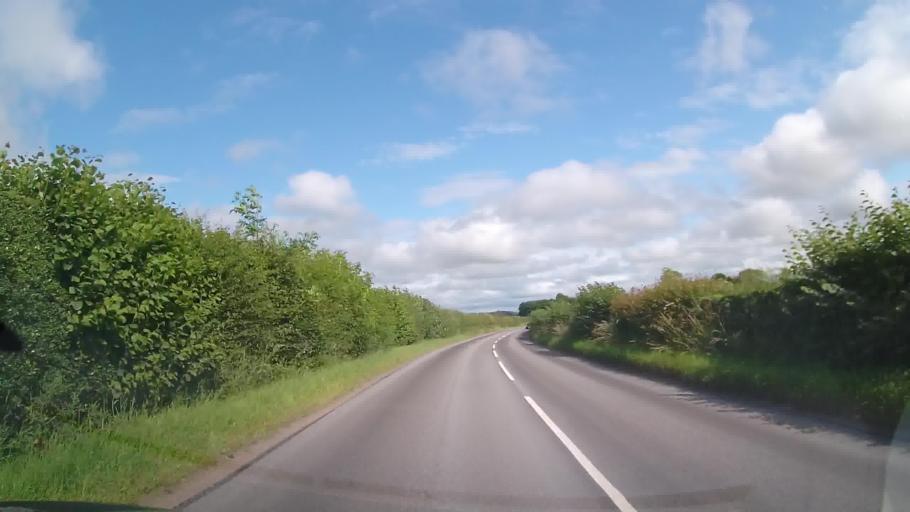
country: GB
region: England
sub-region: Shropshire
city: Pant
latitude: 52.8100
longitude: -3.0358
